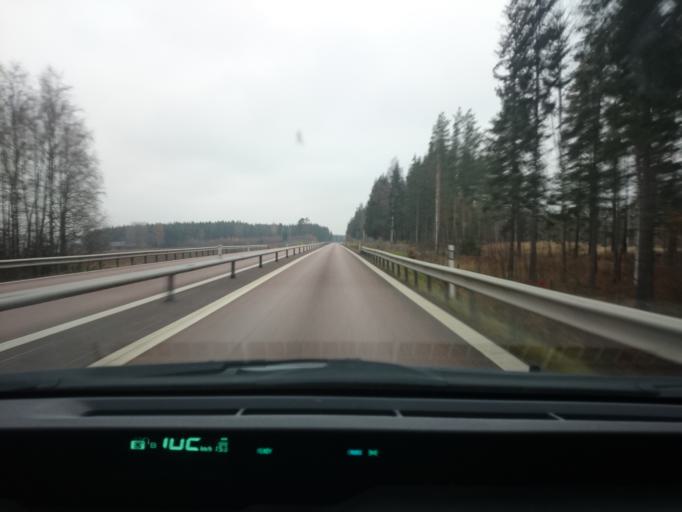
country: SE
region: Dalarna
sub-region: Hedemora Kommun
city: Hedemora
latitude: 60.3208
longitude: 15.9011
